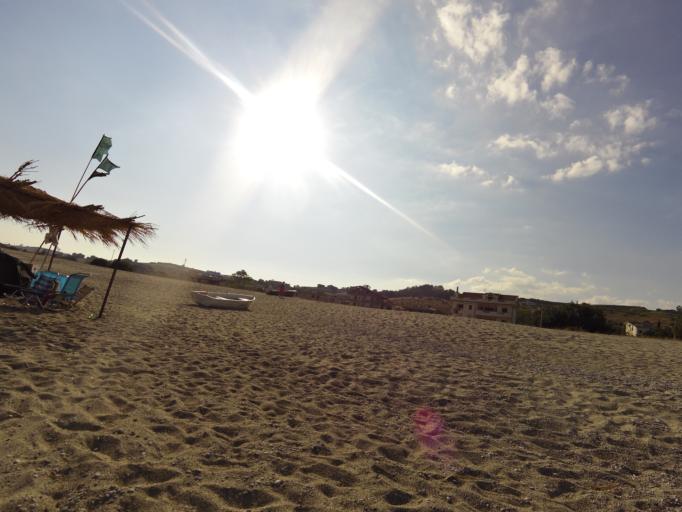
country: IT
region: Calabria
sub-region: Provincia di Reggio Calabria
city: Riace Marina
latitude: 38.3969
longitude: 16.5400
